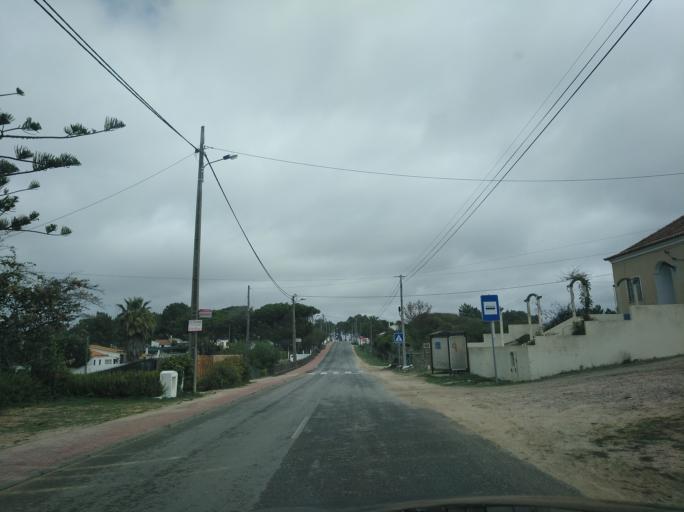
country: PT
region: Setubal
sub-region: Santiago do Cacem
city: Santo Andre
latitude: 38.1296
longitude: -8.7853
